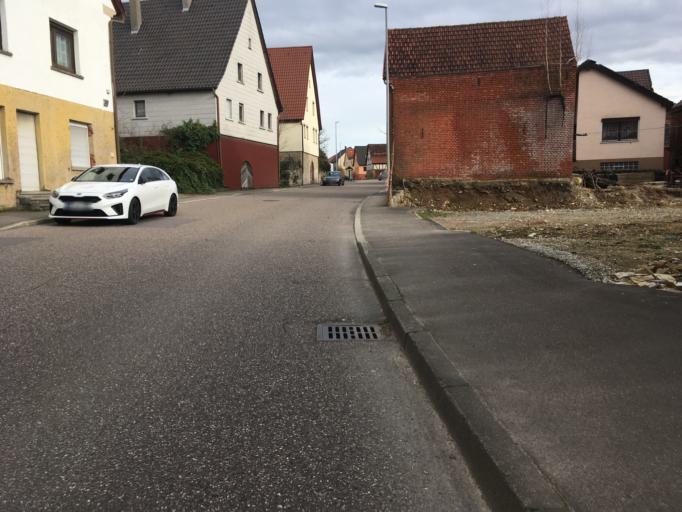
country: DE
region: Baden-Wuerttemberg
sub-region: Regierungsbezirk Stuttgart
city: Bretzfeld
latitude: 49.2142
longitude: 9.4111
